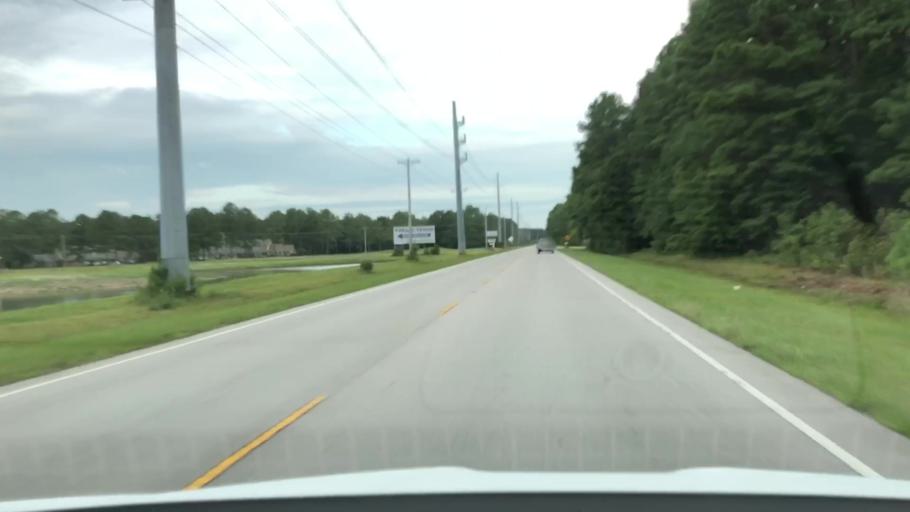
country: US
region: North Carolina
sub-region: Carteret County
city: Cape Carteret
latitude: 34.7376
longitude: -77.0838
